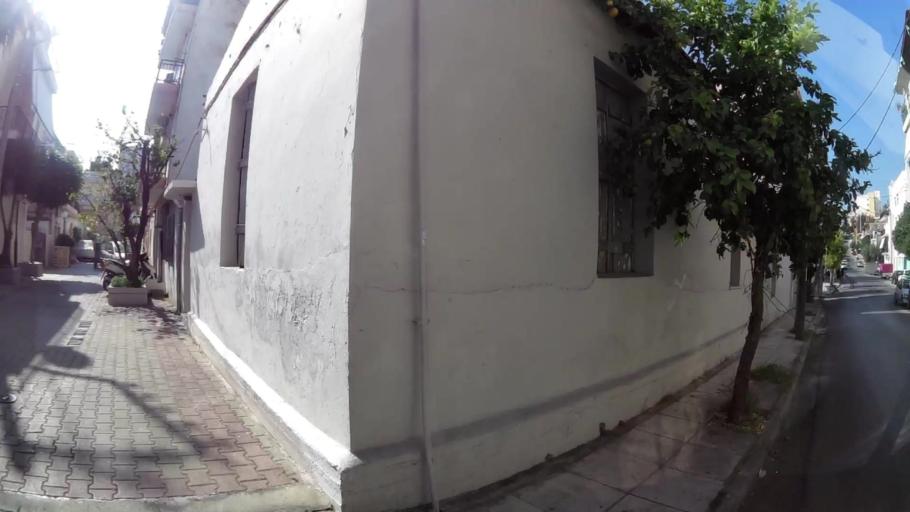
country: GR
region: Attica
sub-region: Nomos Piraios
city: Drapetsona
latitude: 37.9512
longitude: 23.6214
